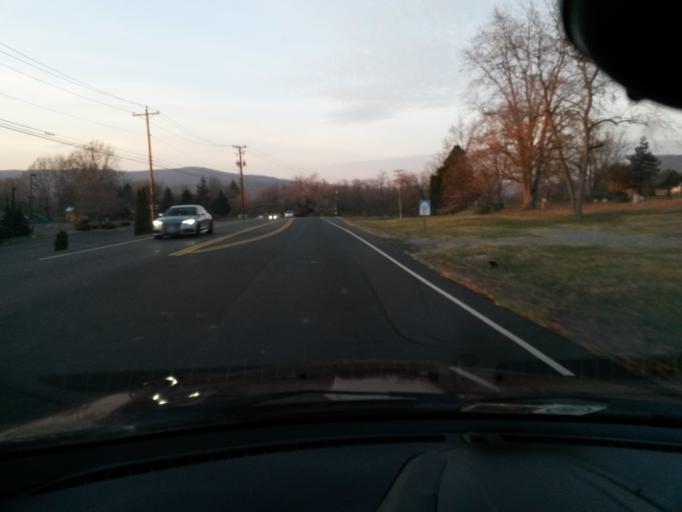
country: US
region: Virginia
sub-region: Roanoke County
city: Hollins
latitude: 37.3396
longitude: -79.9423
